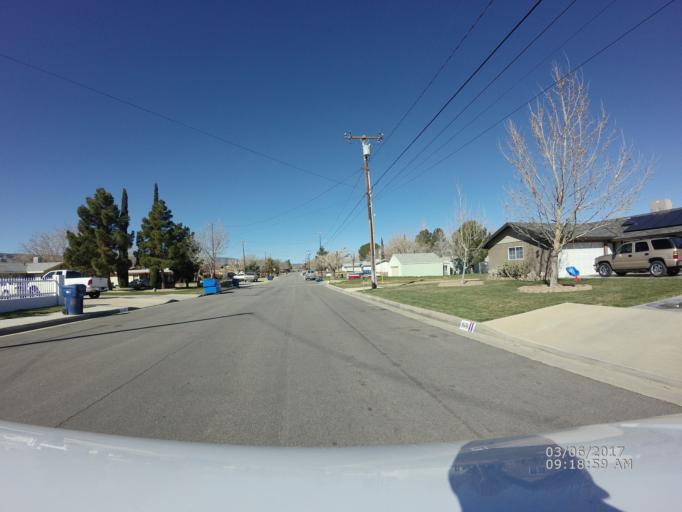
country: US
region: California
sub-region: Los Angeles County
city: Quartz Hill
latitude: 34.6547
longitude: -118.2068
